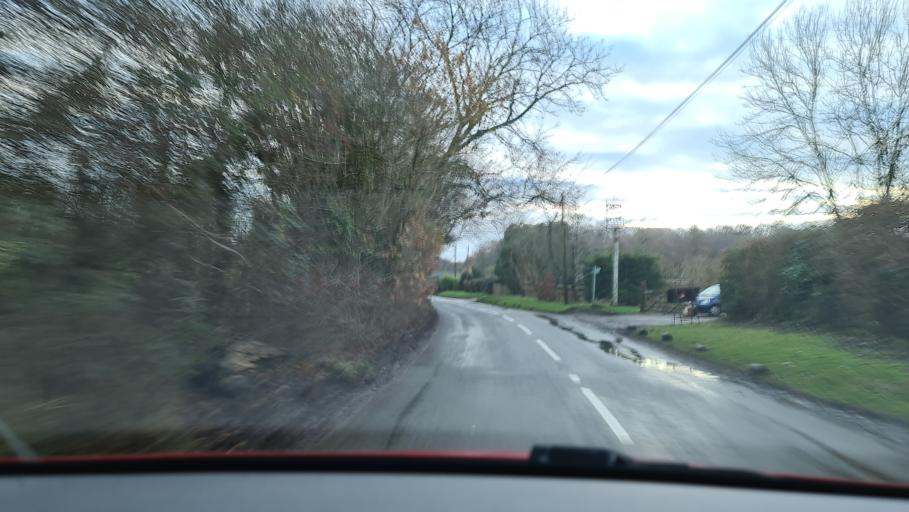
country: GB
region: England
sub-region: Buckinghamshire
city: Great Missenden
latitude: 51.7407
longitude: -0.7041
